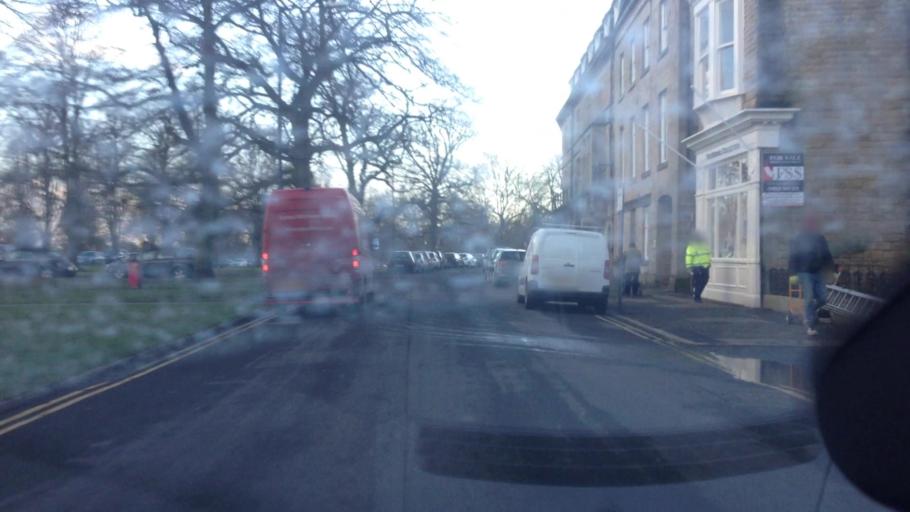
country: GB
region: England
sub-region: North Yorkshire
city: Harrogate
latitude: 53.9954
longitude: -1.5274
